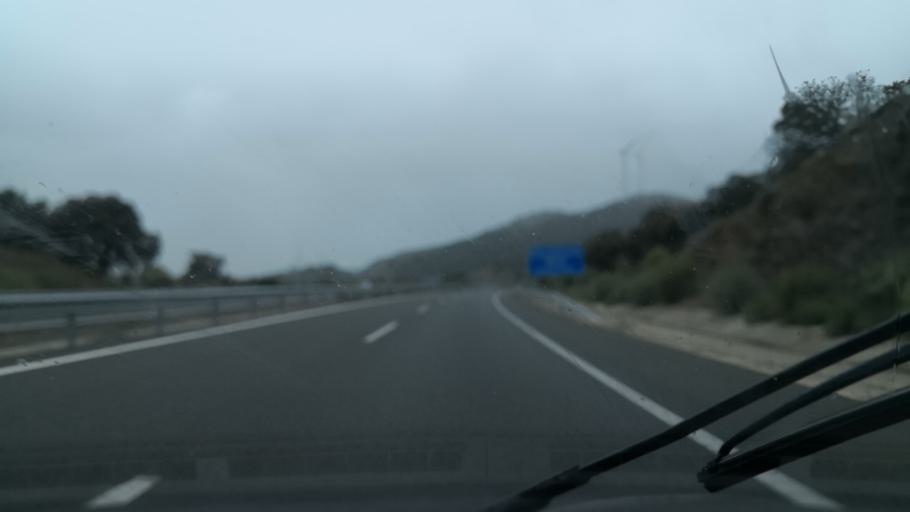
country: ES
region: Extremadura
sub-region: Provincia de Caceres
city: Plasencia
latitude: 40.0256
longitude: -6.1228
